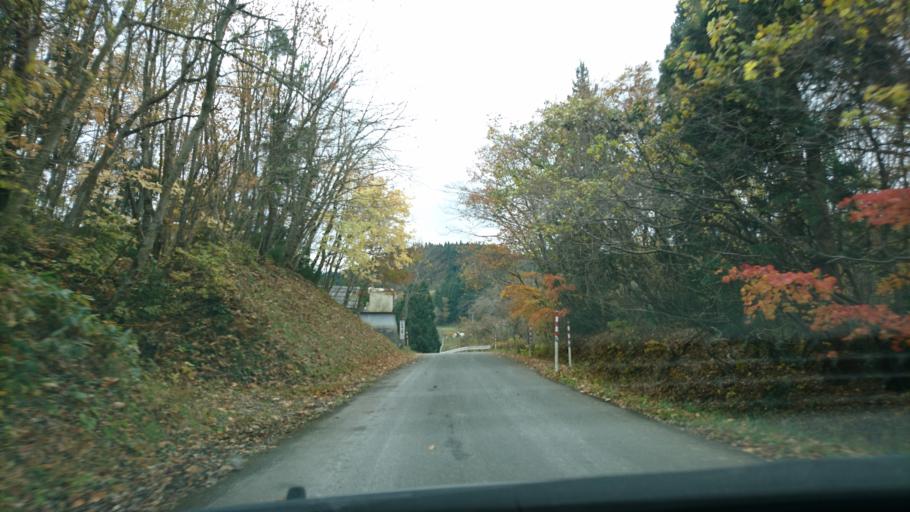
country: JP
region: Iwate
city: Ichinoseki
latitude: 39.0087
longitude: 141.2162
